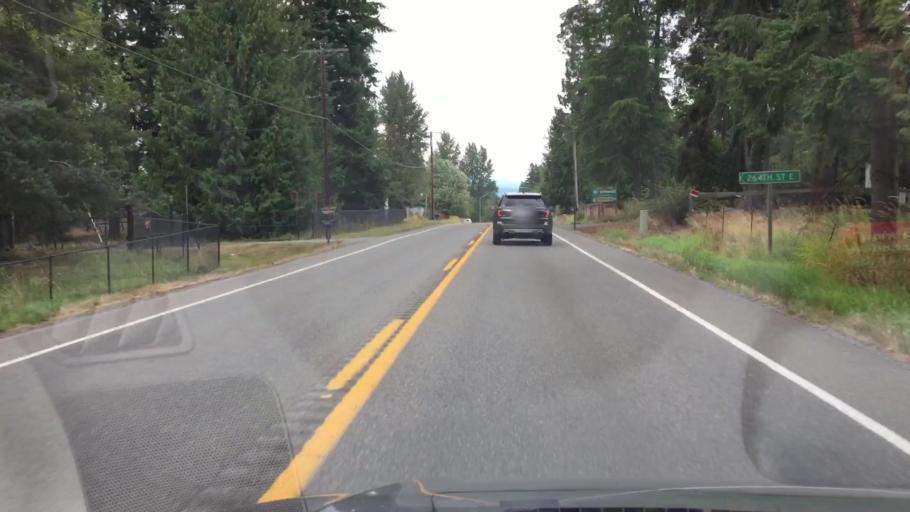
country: US
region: Washington
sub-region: Pierce County
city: Graham
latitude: 47.0192
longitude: -122.2963
